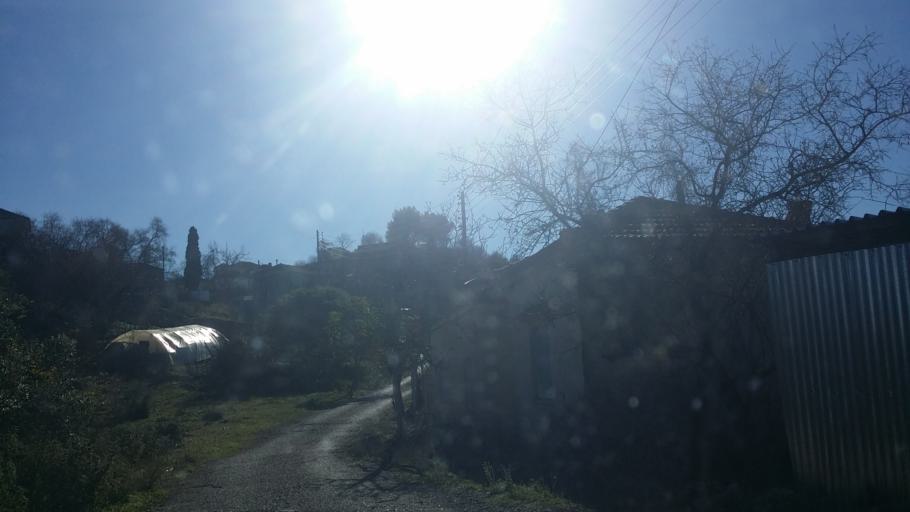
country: GR
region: West Greece
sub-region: Nomos Aitolias kai Akarnanias
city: Fitiai
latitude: 38.7127
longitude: 21.1734
